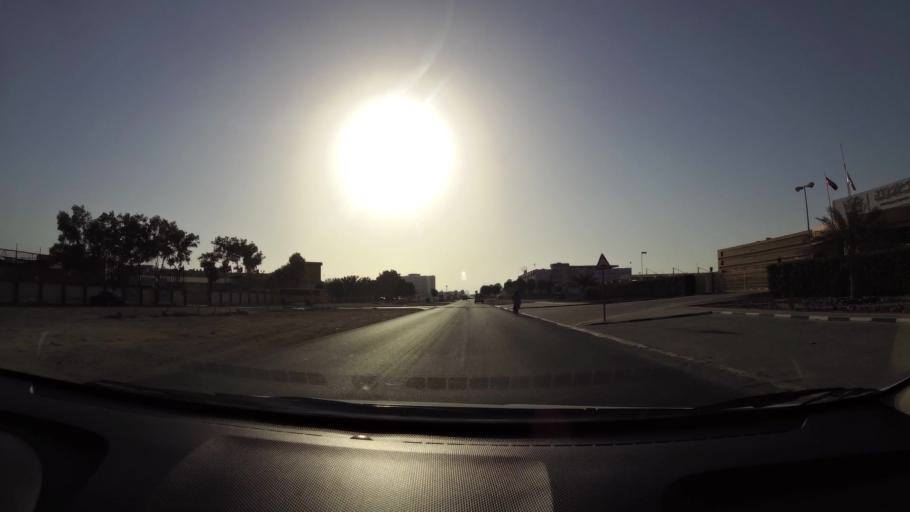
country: AE
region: Ajman
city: Ajman
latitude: 25.3998
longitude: 55.4943
